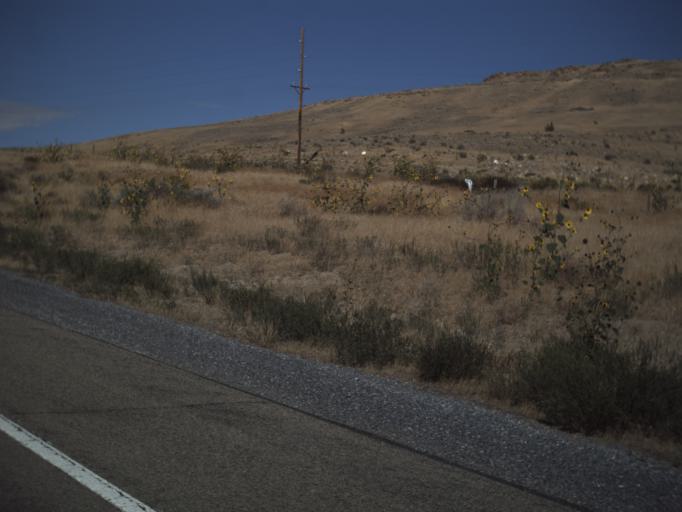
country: US
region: Utah
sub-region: Tooele County
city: Grantsville
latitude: 40.8228
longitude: -112.9013
